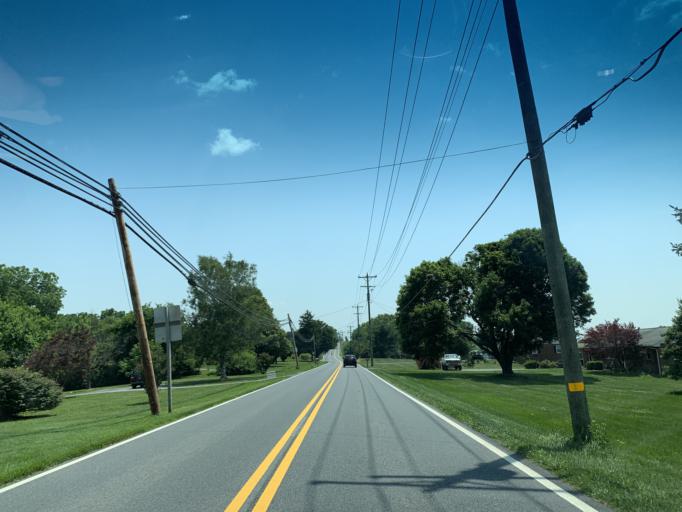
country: US
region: Maryland
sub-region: Frederick County
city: Green Valley
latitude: 39.3577
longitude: -77.2696
